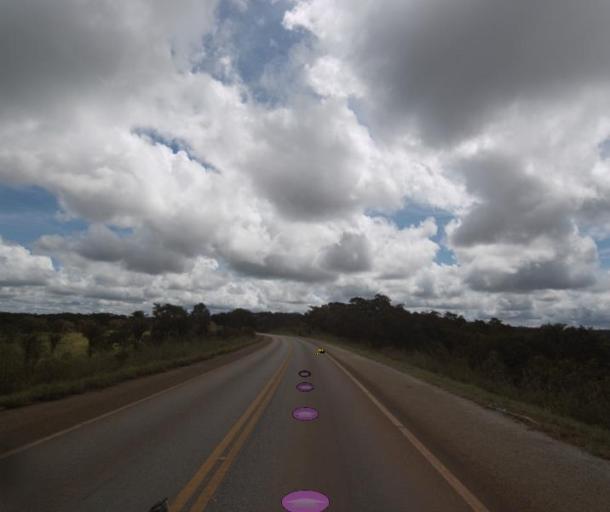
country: BR
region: Goias
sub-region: Pirenopolis
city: Pirenopolis
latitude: -15.7624
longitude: -48.5728
